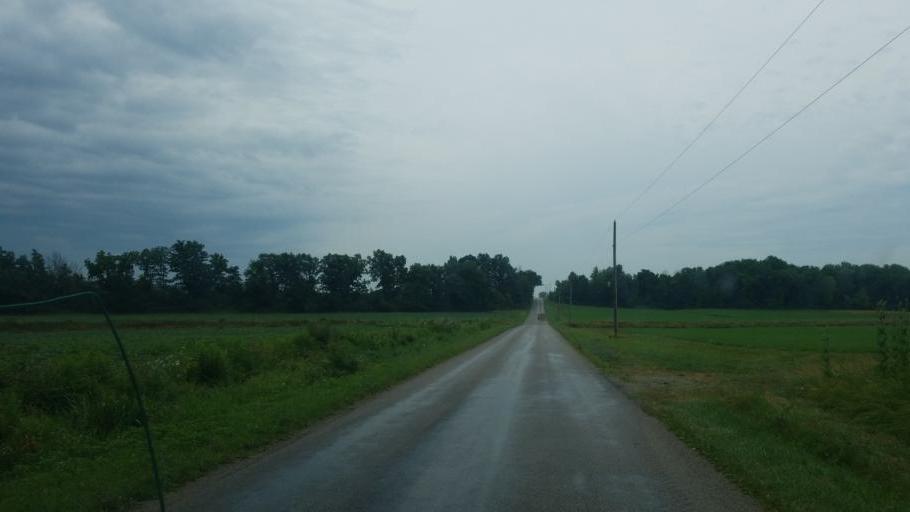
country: US
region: Ohio
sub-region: Williams County
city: Edgerton
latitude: 41.4338
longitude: -84.6703
